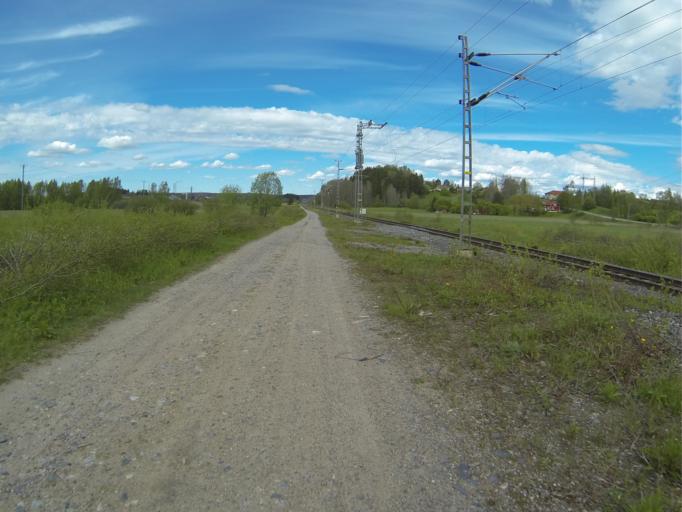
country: FI
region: Varsinais-Suomi
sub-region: Salo
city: Salo
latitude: 60.3571
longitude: 23.1173
